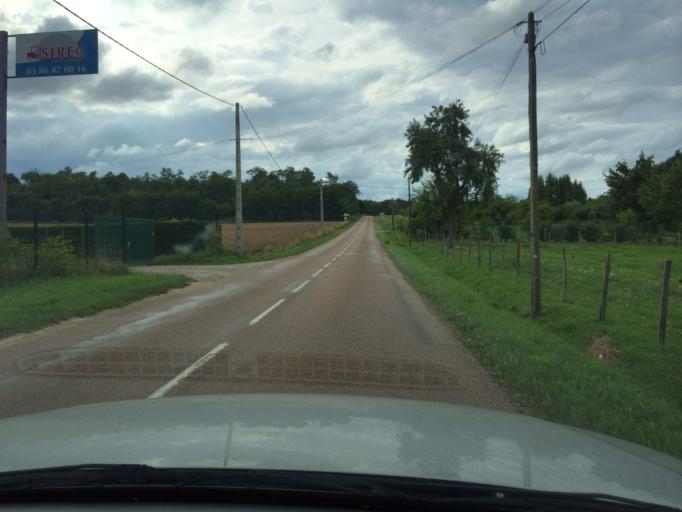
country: FR
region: Bourgogne
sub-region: Departement de l'Yonne
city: Charbuy
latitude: 47.8475
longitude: 3.4804
